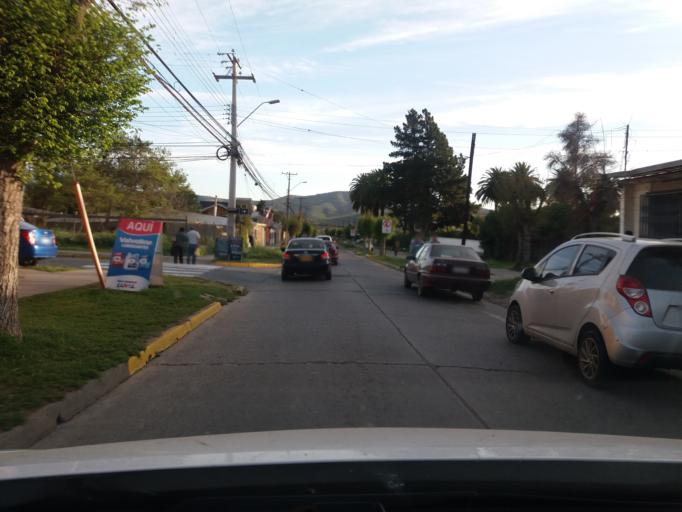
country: CL
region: Valparaiso
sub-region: Provincia de Marga Marga
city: Limache
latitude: -32.9857
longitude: -71.2777
